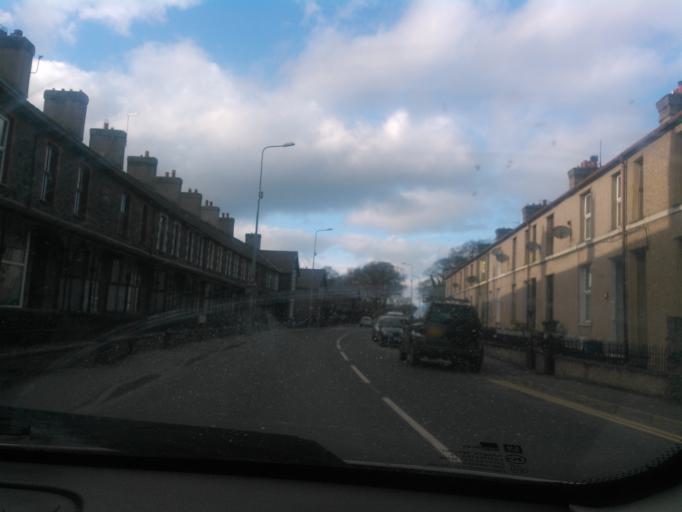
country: GB
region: Wales
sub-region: Gwynedd
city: Bethesda
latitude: 53.1817
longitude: -4.0670
